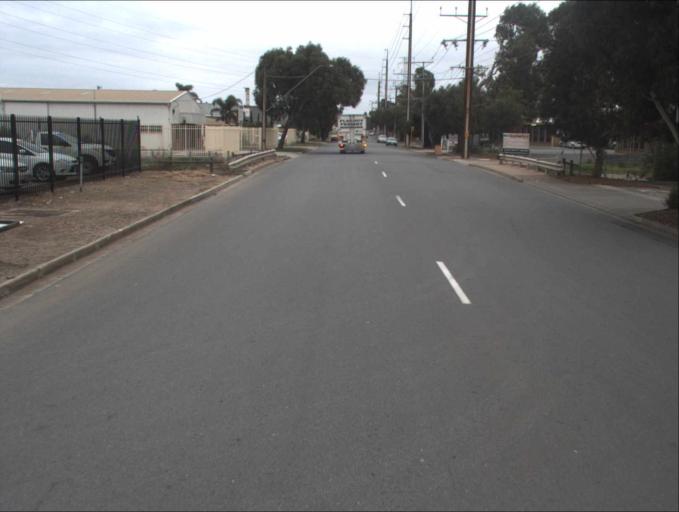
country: AU
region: South Australia
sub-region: Port Adelaide Enfield
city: Blair Athol
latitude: -34.8452
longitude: 138.5822
